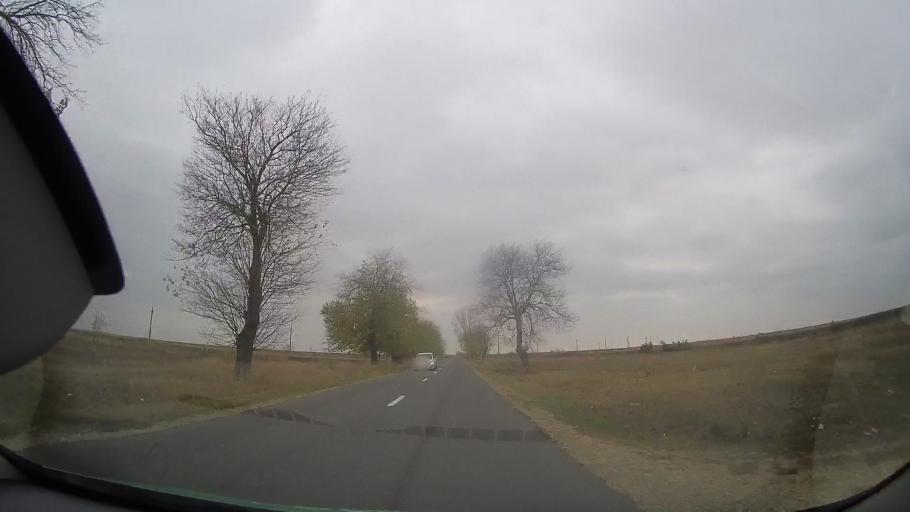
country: RO
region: Ialomita
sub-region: Comuna Garbovi
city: Garbovi
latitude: 44.7758
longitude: 26.7495
